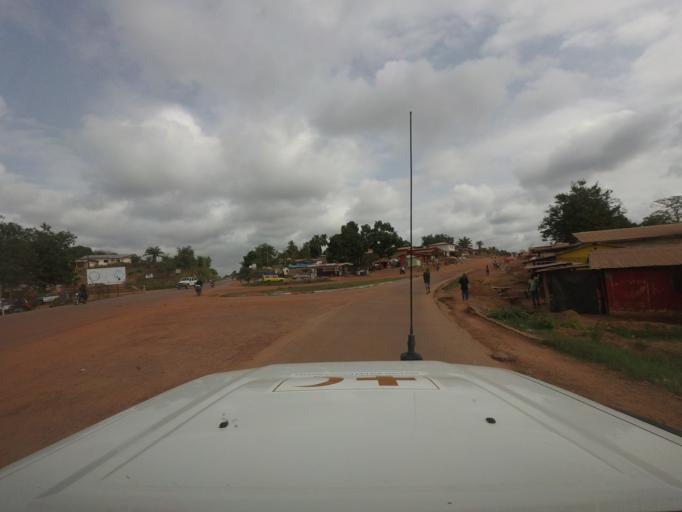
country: LR
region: Bong
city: Gbarnga
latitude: 7.0070
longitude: -9.4796
